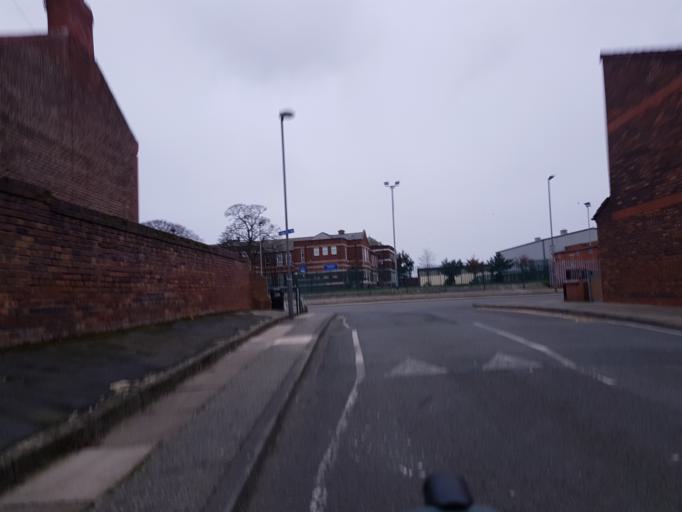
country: GB
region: England
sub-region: Sefton
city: Litherland
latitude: 53.4486
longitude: -2.9730
